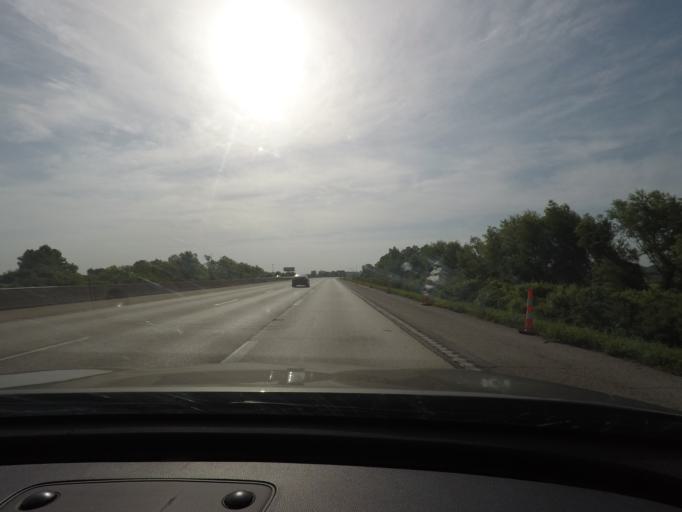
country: US
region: Missouri
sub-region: Saint Louis County
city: Bridgeton
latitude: 38.7900
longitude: -90.4291
